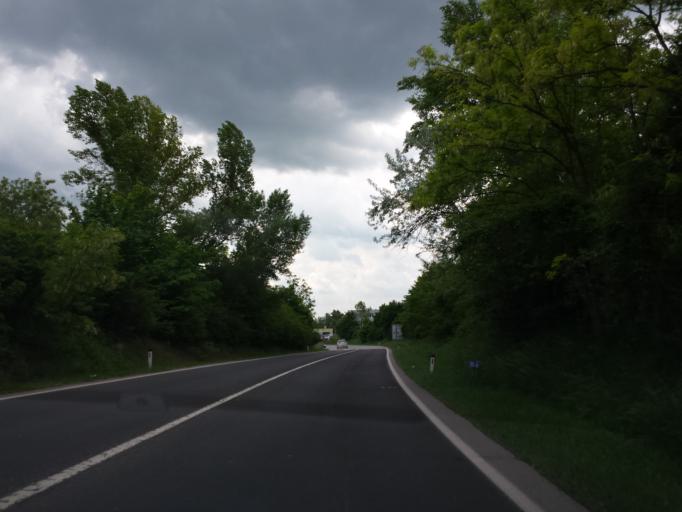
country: AT
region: Lower Austria
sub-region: Politischer Bezirk Wien-Umgebung
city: Fischamend Dorf
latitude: 48.1235
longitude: 16.5972
